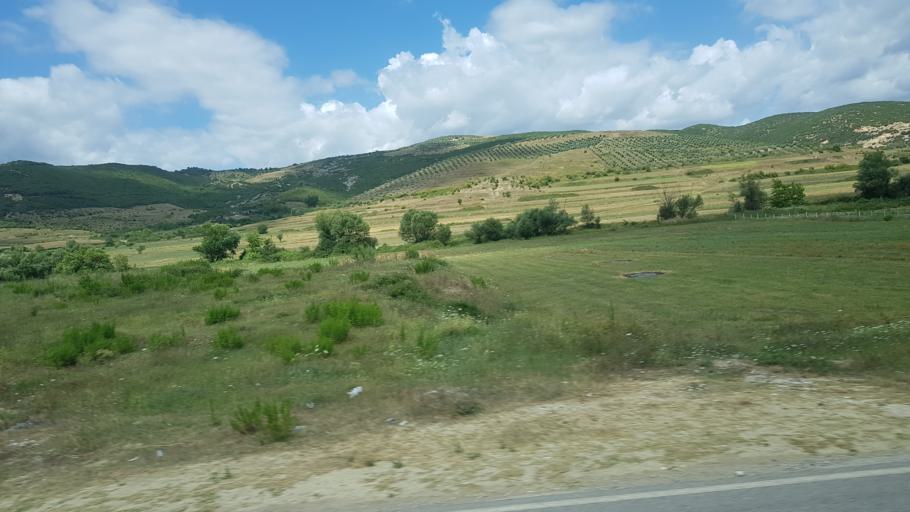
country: AL
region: Gjirokaster
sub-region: Rrethi i Tepelenes
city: Krahes
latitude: 40.4197
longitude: 19.8578
